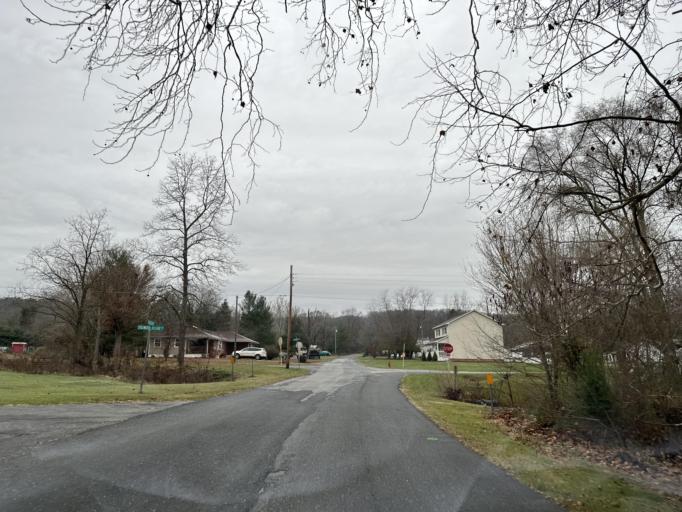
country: US
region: Virginia
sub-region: Rockbridge County
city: East Lexington
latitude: 38.0770
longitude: -79.3922
